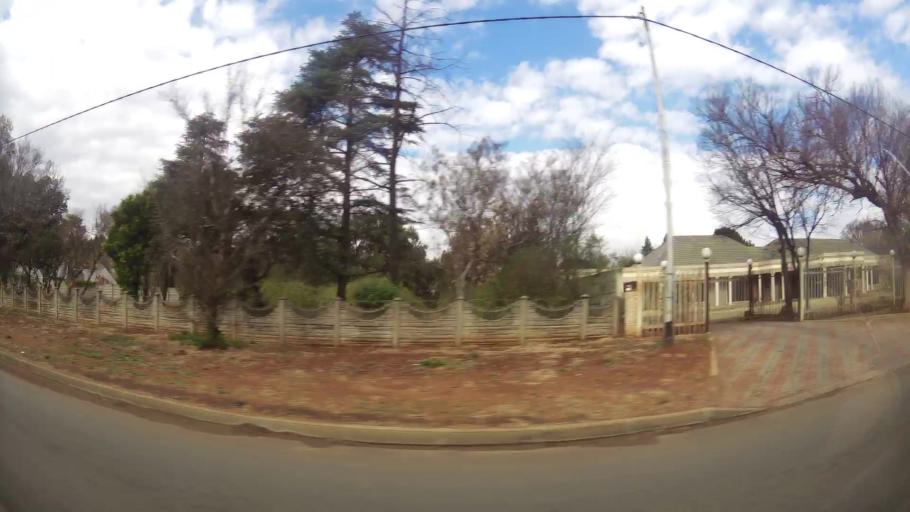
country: ZA
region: Gauteng
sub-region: Sedibeng District Municipality
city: Vereeniging
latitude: -26.6569
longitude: 27.9936
